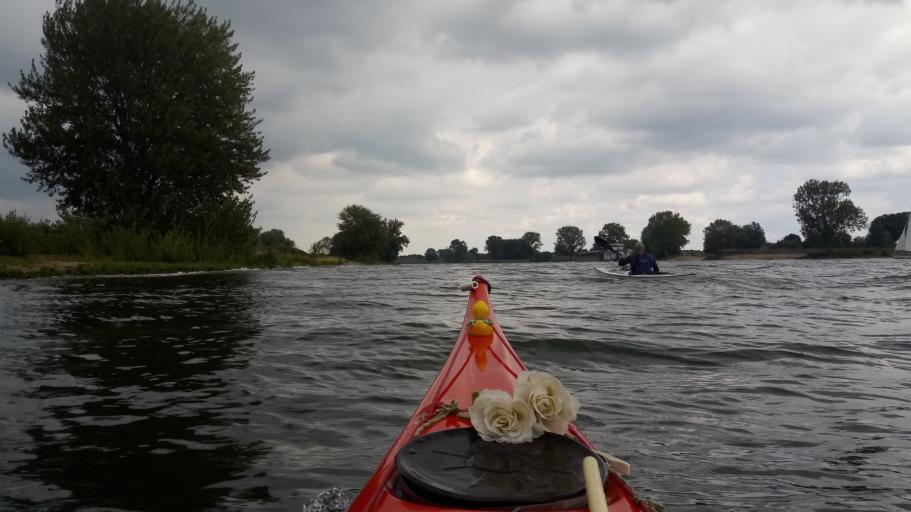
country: NL
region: North Brabant
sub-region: Gemeente 's-Hertogenbosch
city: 's-Hertogenbosch
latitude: 51.7530
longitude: 5.3430
